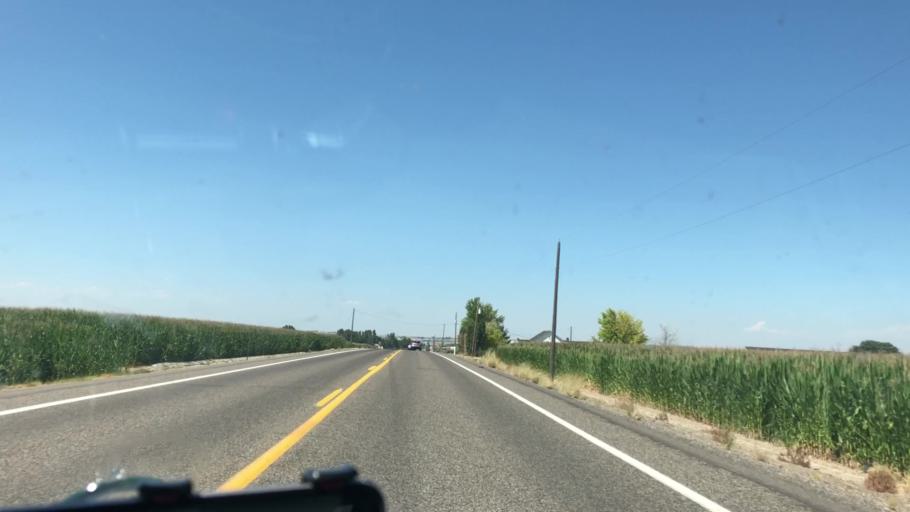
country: US
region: Idaho
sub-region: Owyhee County
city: Marsing
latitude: 43.5391
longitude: -116.8516
